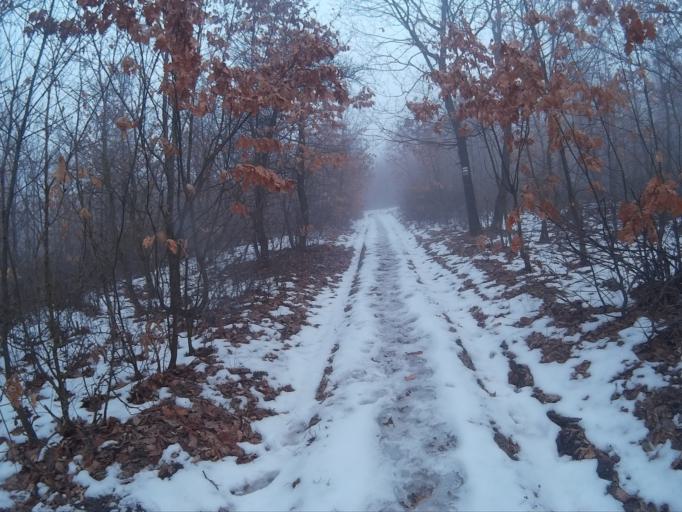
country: HU
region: Nograd
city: Matraverebely
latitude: 47.9873
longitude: 19.7624
